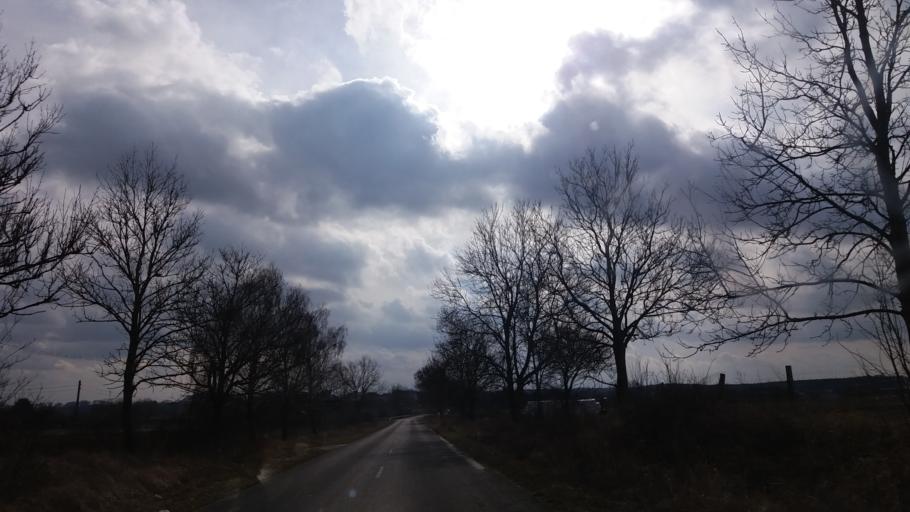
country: PL
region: West Pomeranian Voivodeship
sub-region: Powiat choszczenski
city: Drawno
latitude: 53.2292
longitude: 15.7510
